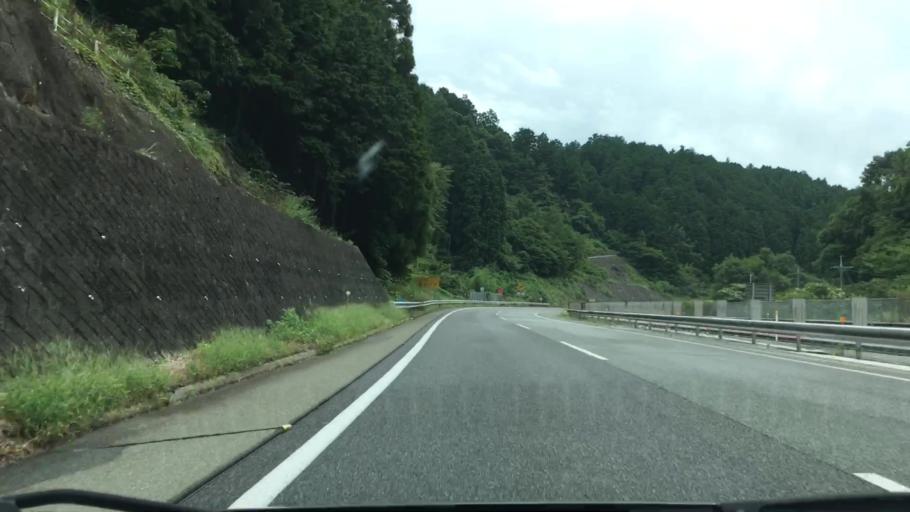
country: JP
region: Hiroshima
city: Shobara
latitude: 34.8938
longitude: 133.2257
